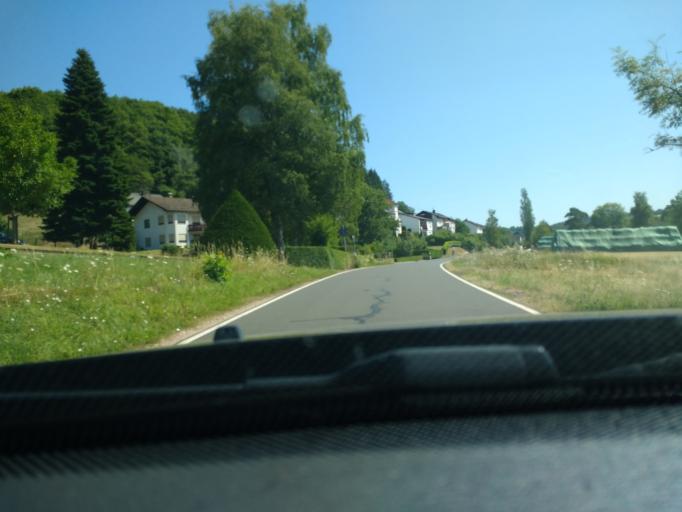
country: DE
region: Rheinland-Pfalz
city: Flussbach
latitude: 50.0160
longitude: 6.9191
